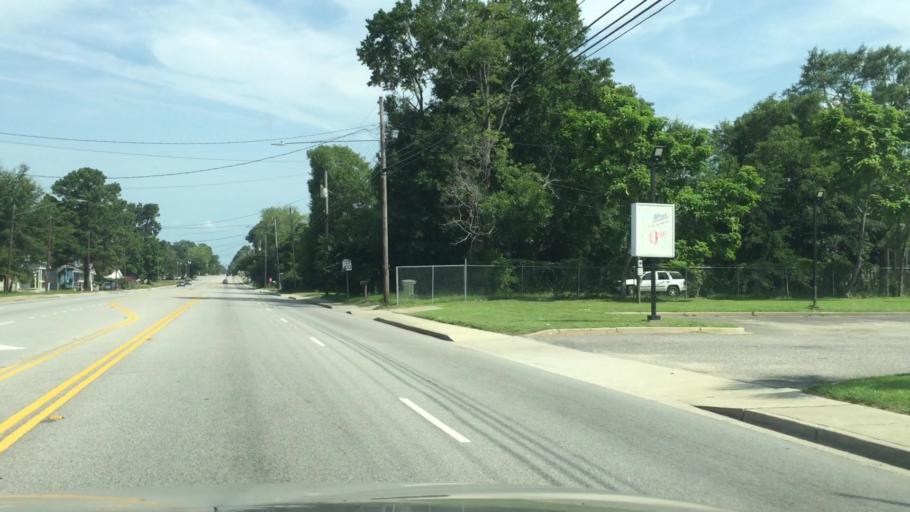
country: US
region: South Carolina
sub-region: Sumter County
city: South Sumter
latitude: 33.9158
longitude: -80.3566
